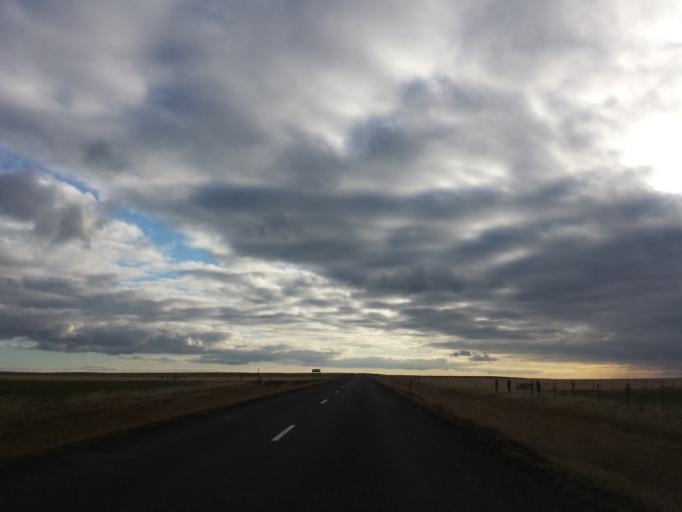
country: IS
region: West
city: Borgarnes
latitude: 64.8012
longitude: -22.2642
